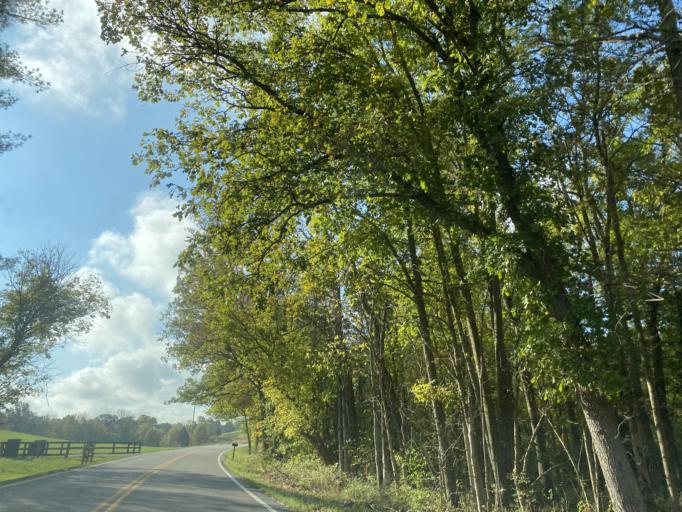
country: US
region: Kentucky
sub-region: Pendleton County
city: Falmouth
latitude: 38.7022
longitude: -84.3044
